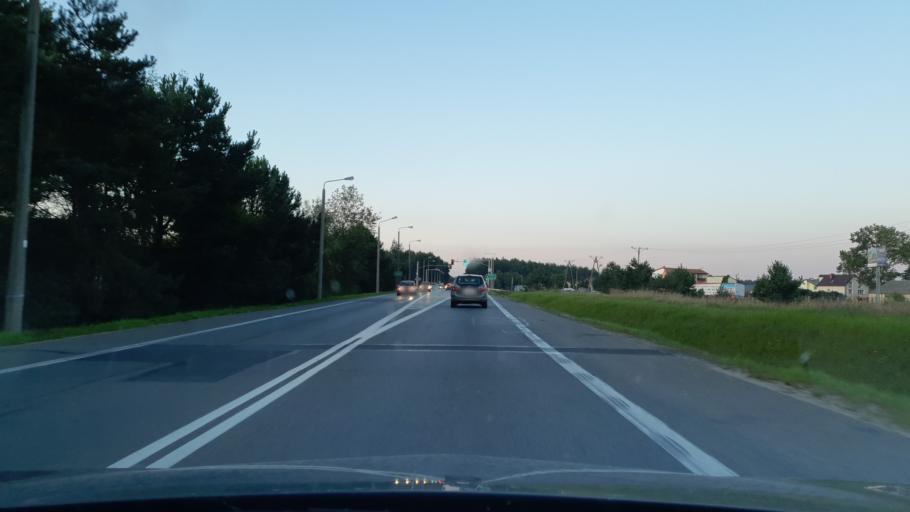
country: PL
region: Pomeranian Voivodeship
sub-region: Powiat leborski
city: Lebork
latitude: 54.5444
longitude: 17.7873
